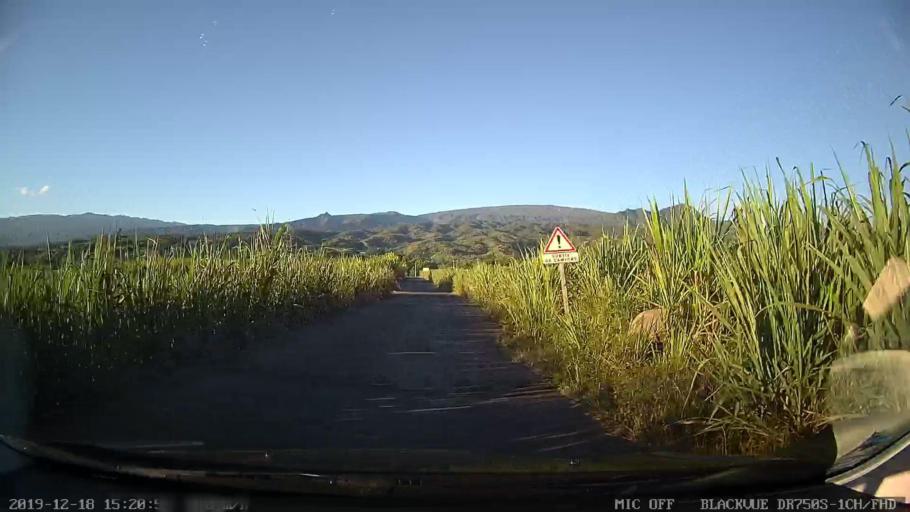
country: RE
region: Reunion
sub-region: Reunion
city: Bras-Panon
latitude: -20.9944
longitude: 55.6629
